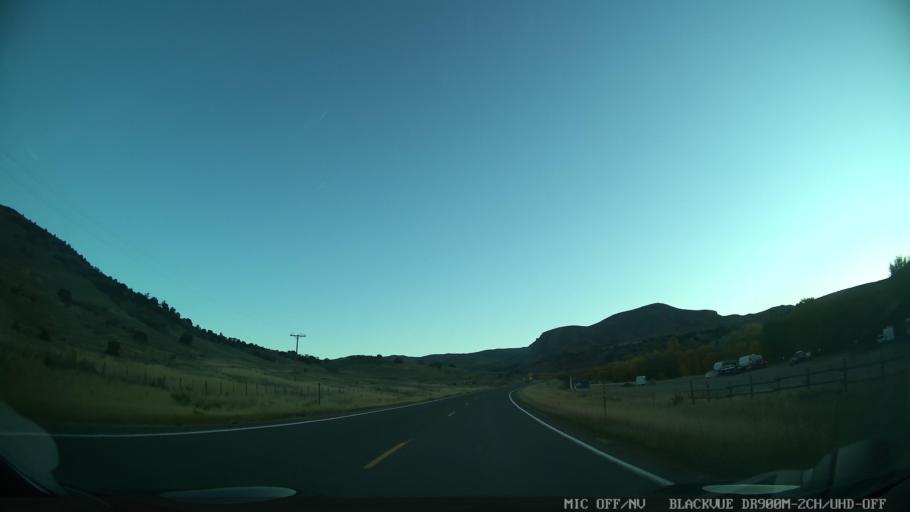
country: US
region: Colorado
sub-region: Eagle County
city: Edwards
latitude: 39.7502
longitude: -106.6742
